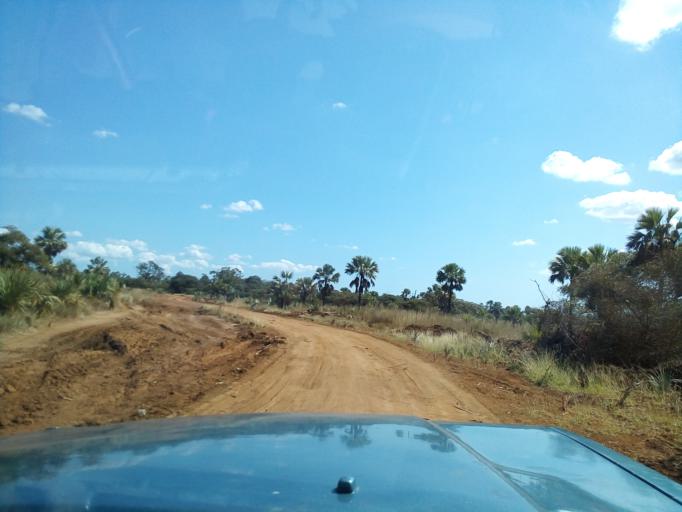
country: MG
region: Boeny
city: Mahajanga
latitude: -15.9695
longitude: 45.9951
